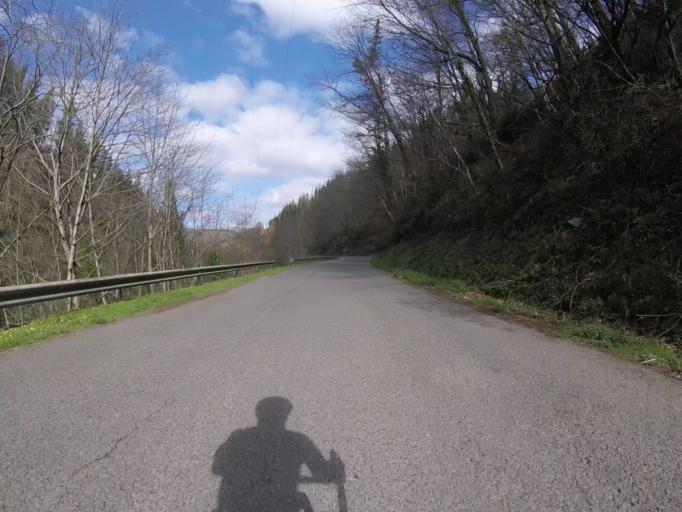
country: ES
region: Navarre
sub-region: Provincia de Navarra
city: Goizueta
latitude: 43.1620
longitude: -1.8516
